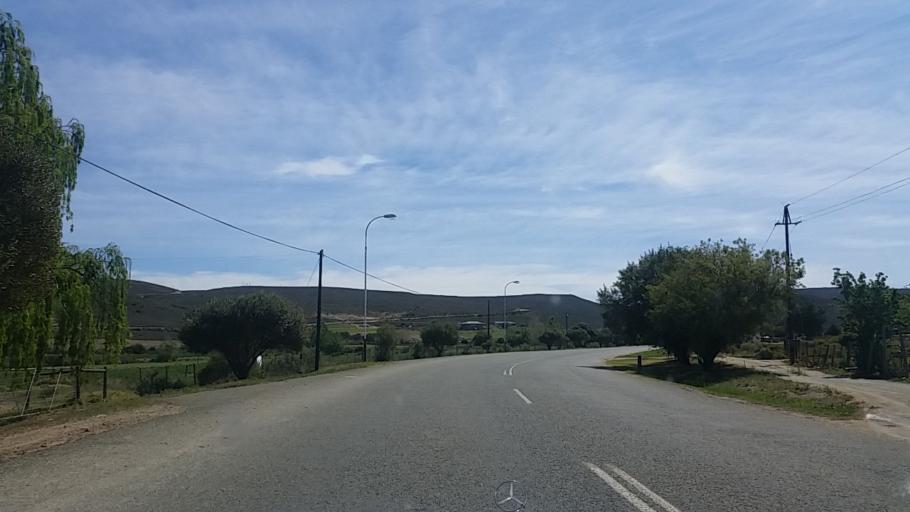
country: ZA
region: Western Cape
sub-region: Eden District Municipality
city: Knysna
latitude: -33.6500
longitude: 23.1346
